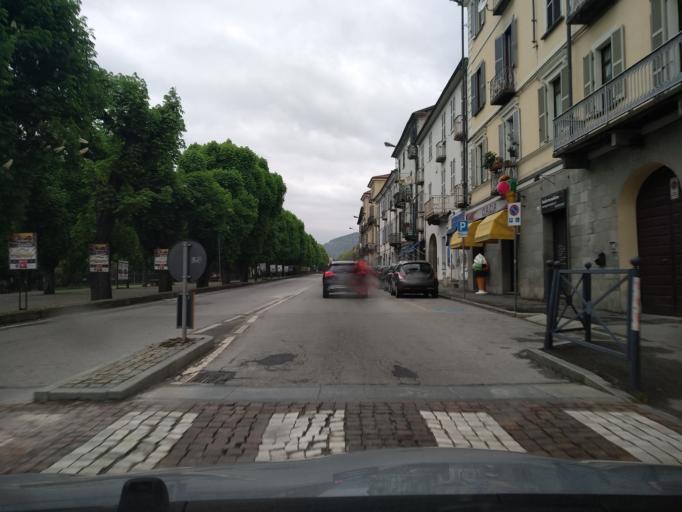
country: IT
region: Piedmont
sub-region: Provincia di Torino
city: Pinerolo
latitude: 44.8849
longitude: 7.3285
